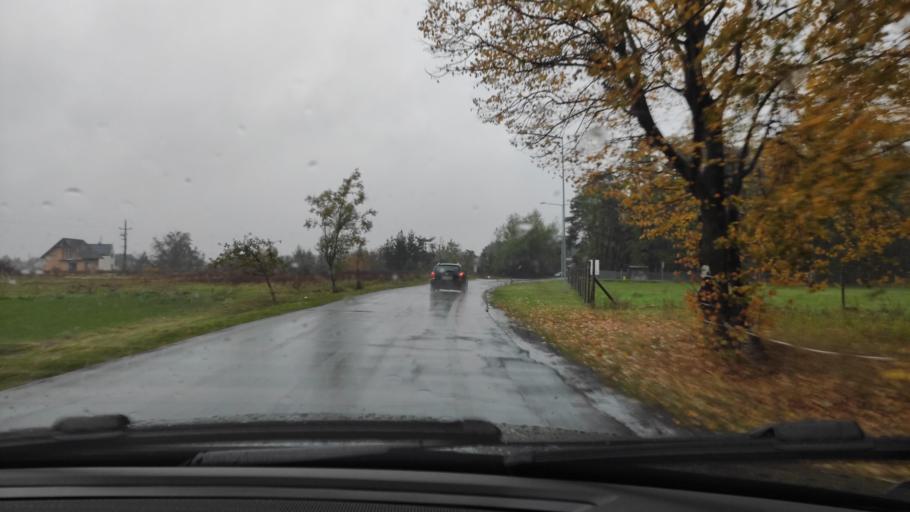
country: PL
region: Greater Poland Voivodeship
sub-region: Powiat poznanski
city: Kornik
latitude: 52.2158
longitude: 17.0983
